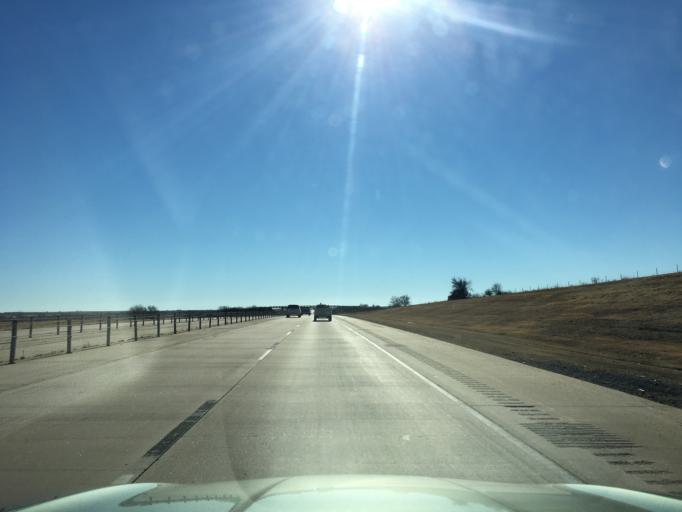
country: US
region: Oklahoma
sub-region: Noble County
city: Perry
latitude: 36.4533
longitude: -97.3271
